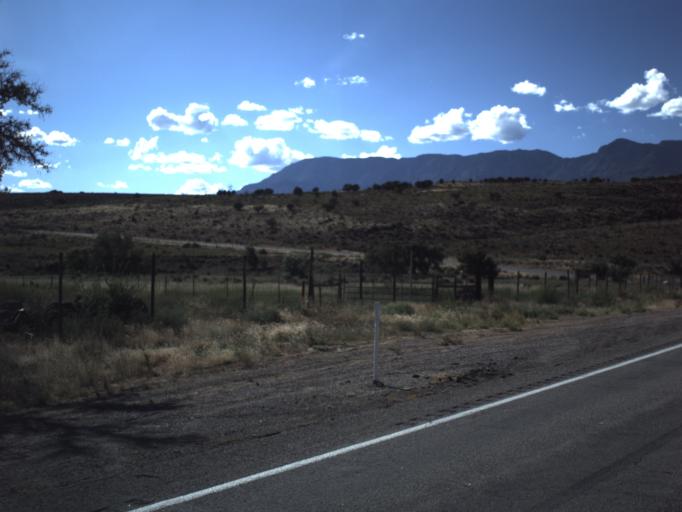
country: US
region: Utah
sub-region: Washington County
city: Toquerville
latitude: 37.2595
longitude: -113.2866
